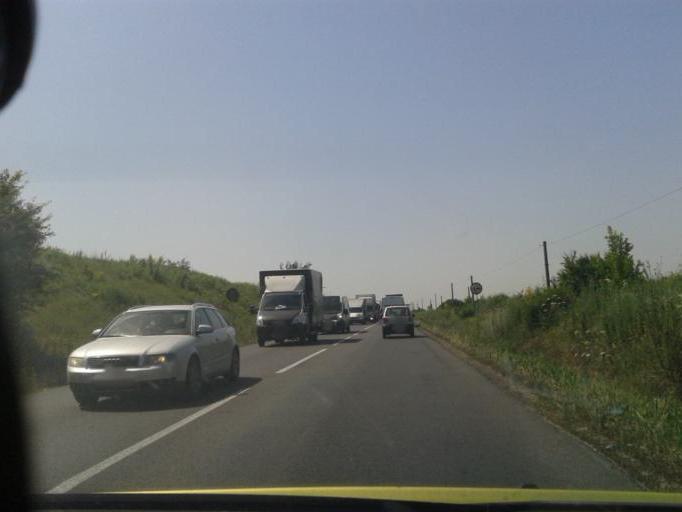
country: RO
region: Ilfov
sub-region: Comuna Glina
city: Catelu
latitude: 44.4311
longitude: 26.2348
